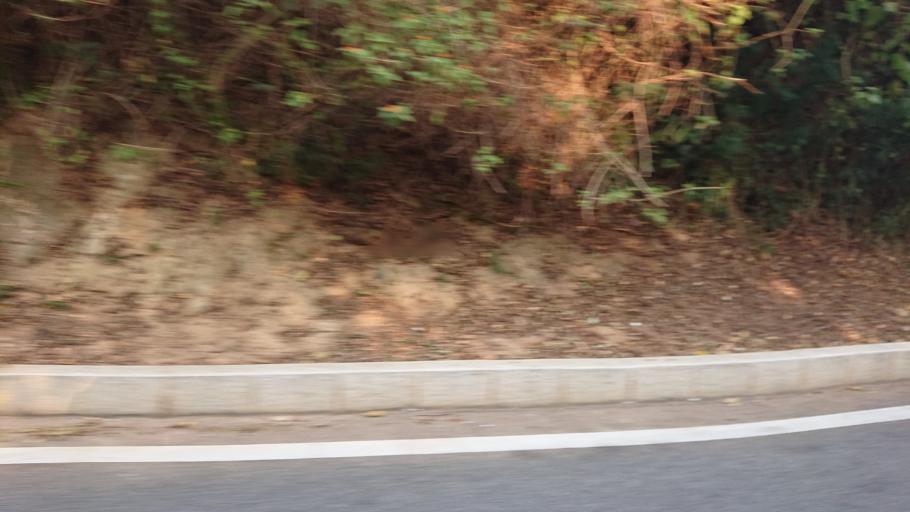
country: TW
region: Fukien
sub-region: Kinmen
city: Jincheng
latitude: 24.4366
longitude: 118.2487
